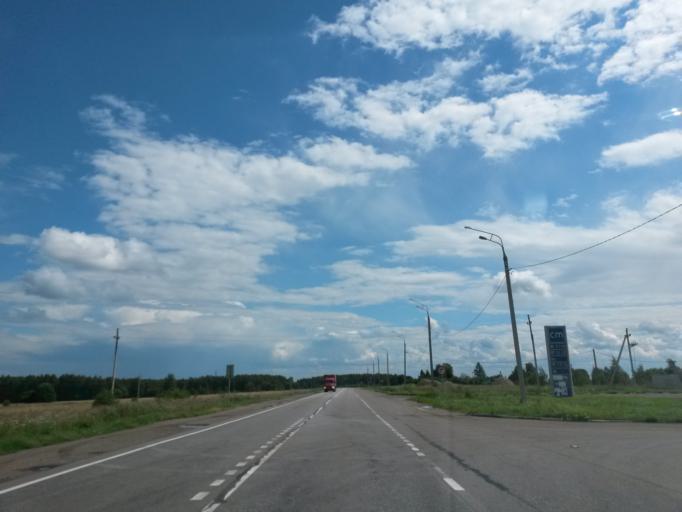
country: RU
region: Jaroslavl
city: Gavrilov-Yam
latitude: 57.2709
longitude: 39.9581
